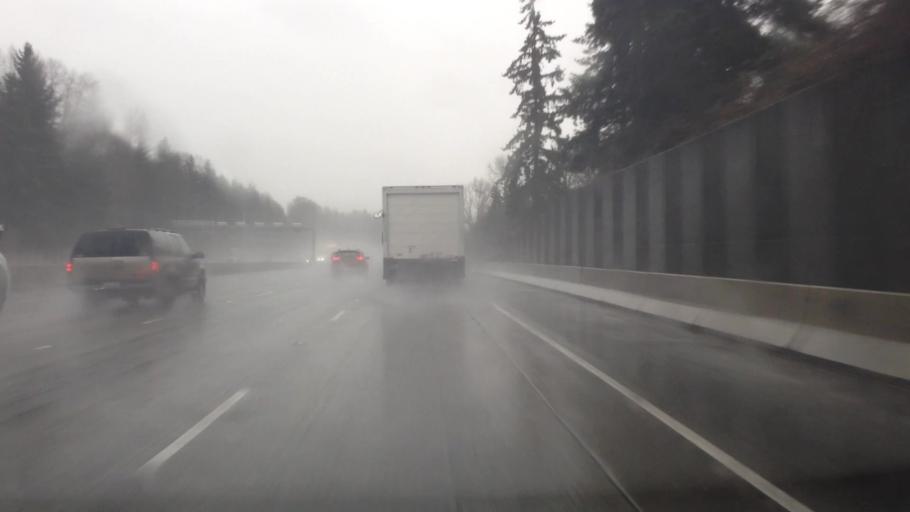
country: US
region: Washington
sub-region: King County
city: Riverton
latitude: 47.4992
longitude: -122.2741
